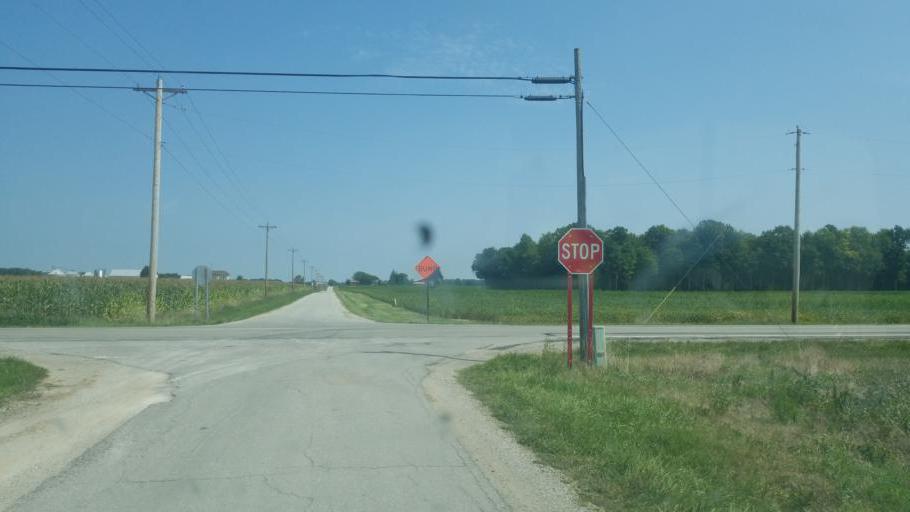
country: US
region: Ohio
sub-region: Crawford County
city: Bucyrus
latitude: 40.9358
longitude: -83.0168
